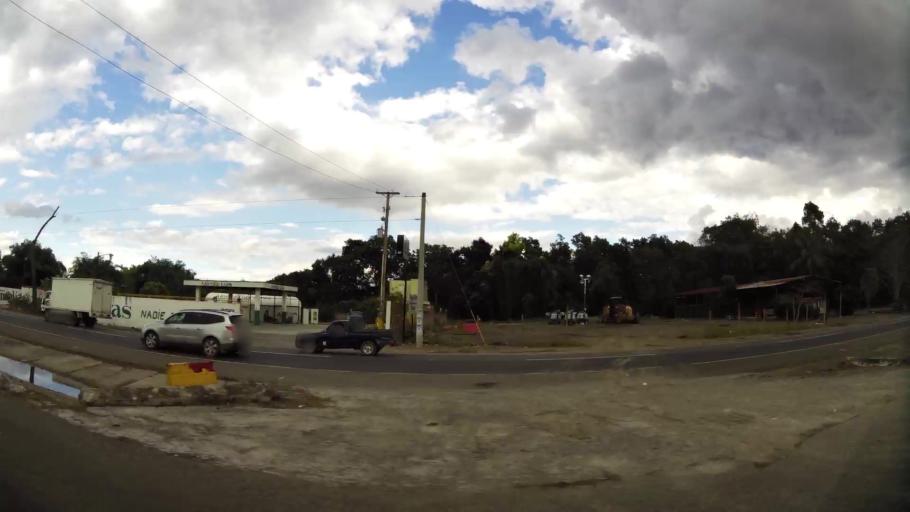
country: DO
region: Monsenor Nouel
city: Sabana del Puerto
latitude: 19.0730
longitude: -70.4458
